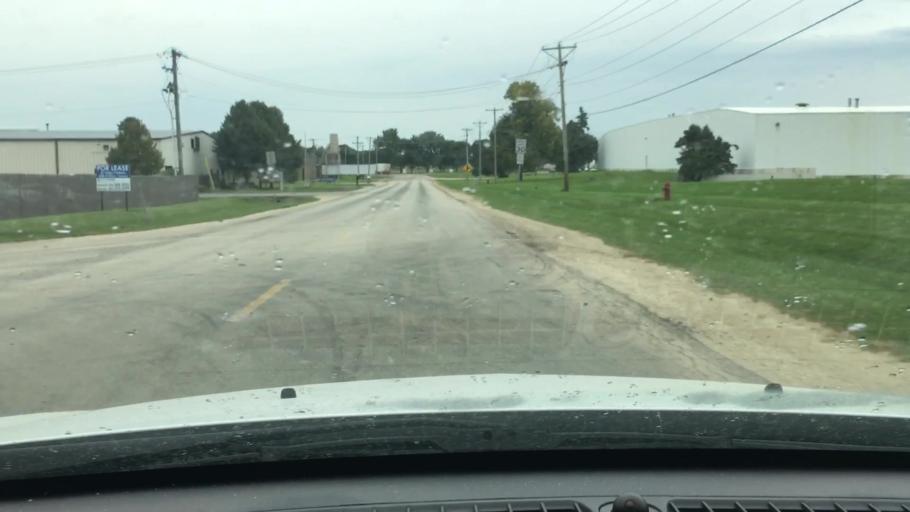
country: US
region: Illinois
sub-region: Ogle County
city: Rochelle
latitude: 41.9057
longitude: -89.0539
